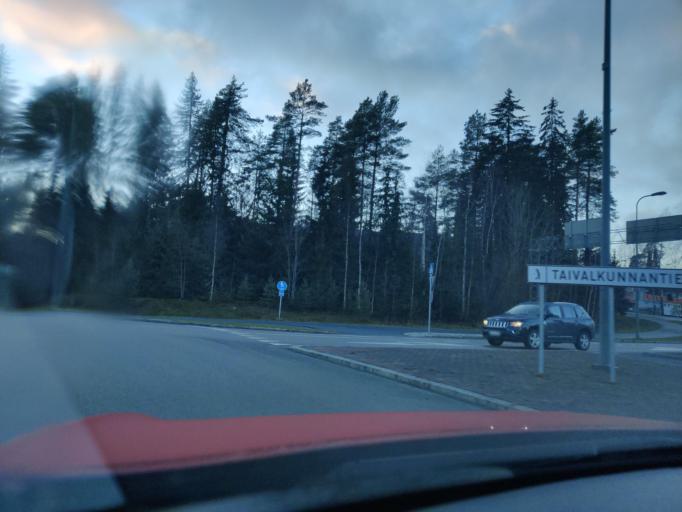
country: FI
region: Pirkanmaa
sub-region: Tampere
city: Nokia
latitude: 61.4688
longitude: 23.5035
